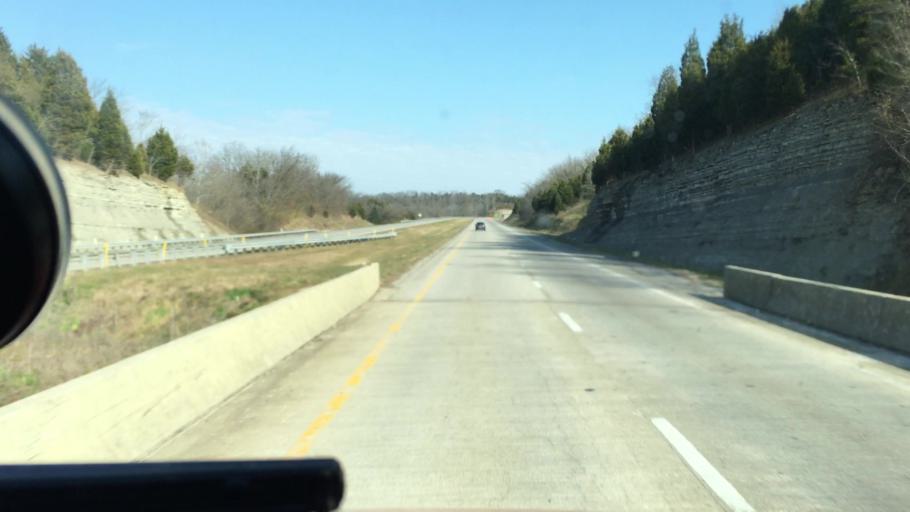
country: US
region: Kentucky
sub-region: Bath County
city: Owingsville
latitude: 38.1185
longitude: -83.7982
